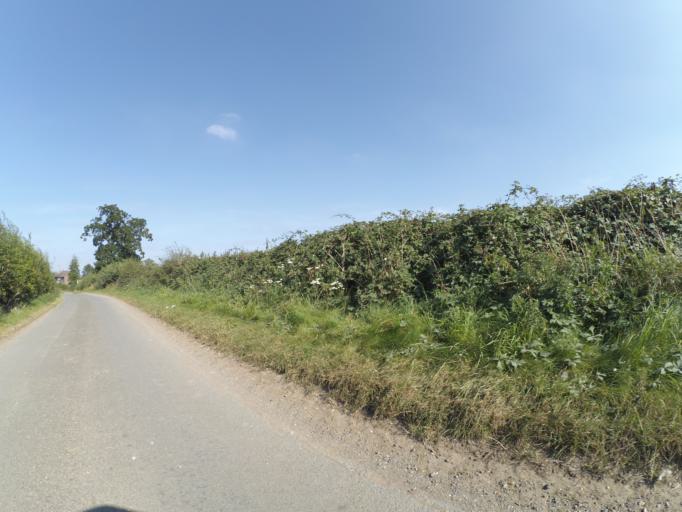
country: GB
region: England
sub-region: Warwickshire
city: Rugby
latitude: 52.4060
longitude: -1.2666
